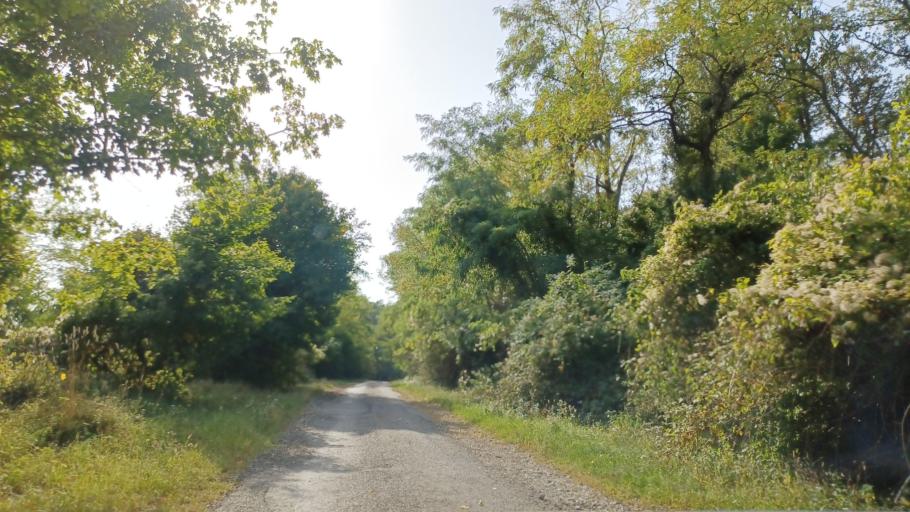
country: HU
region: Baranya
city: Mecseknadasd
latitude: 46.1918
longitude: 18.4490
